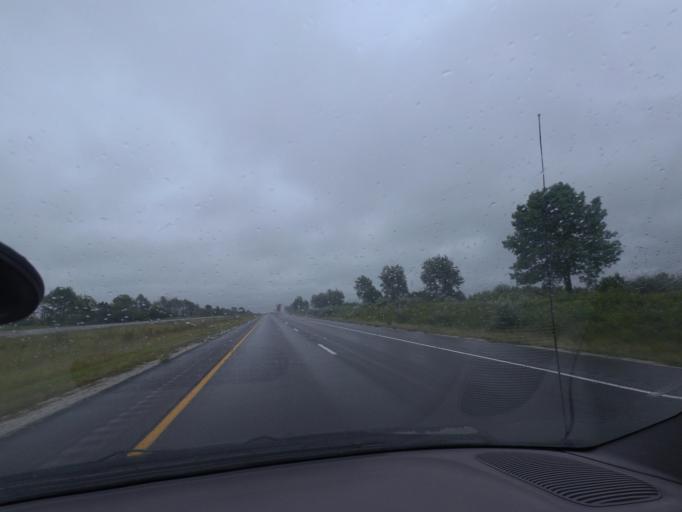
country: US
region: Illinois
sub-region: Scott County
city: Winchester
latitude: 39.6810
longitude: -90.4915
